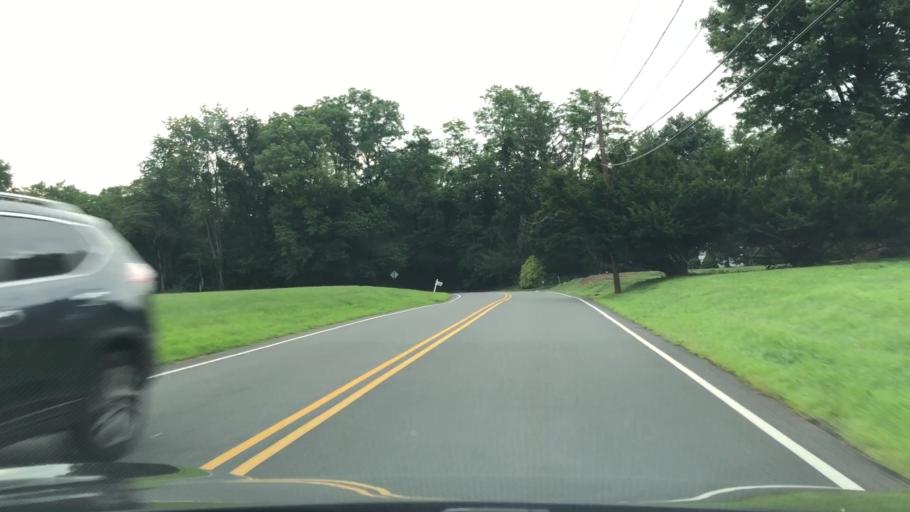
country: US
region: New Jersey
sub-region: Mercer County
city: Lawrenceville
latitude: 40.3085
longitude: -74.7051
